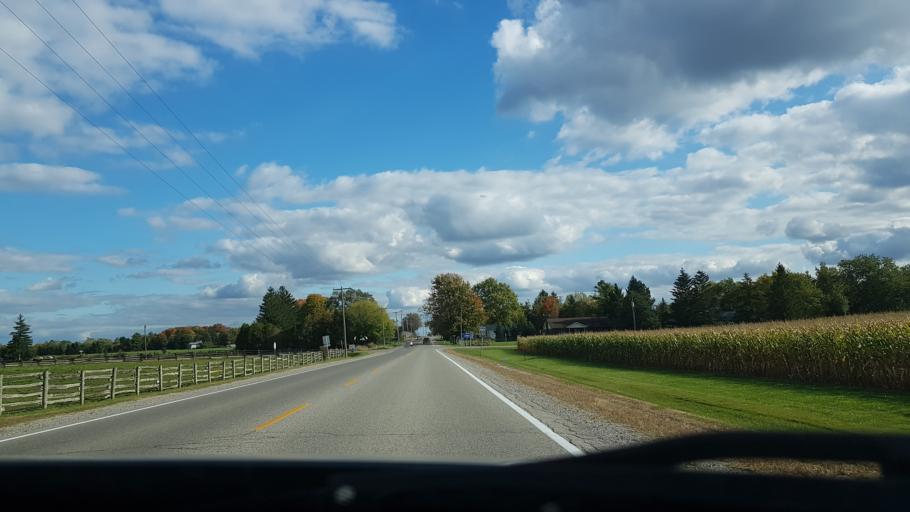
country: CA
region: Ontario
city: Delaware
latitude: 43.0032
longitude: -81.4259
